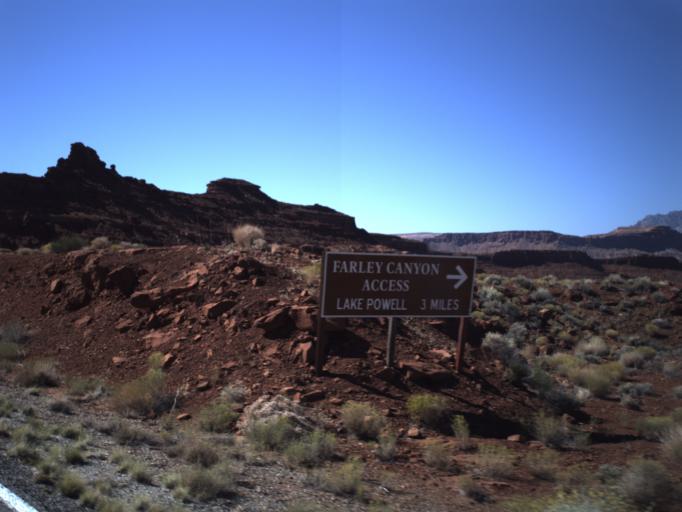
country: US
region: Utah
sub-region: San Juan County
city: Blanding
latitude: 37.8281
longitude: -110.3586
